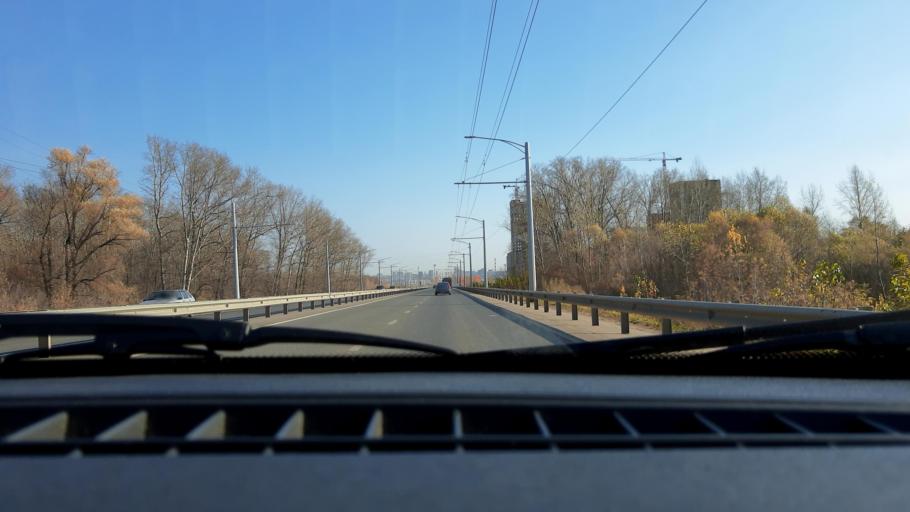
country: RU
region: Bashkortostan
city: Mikhaylovka
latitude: 54.7752
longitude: 55.8943
